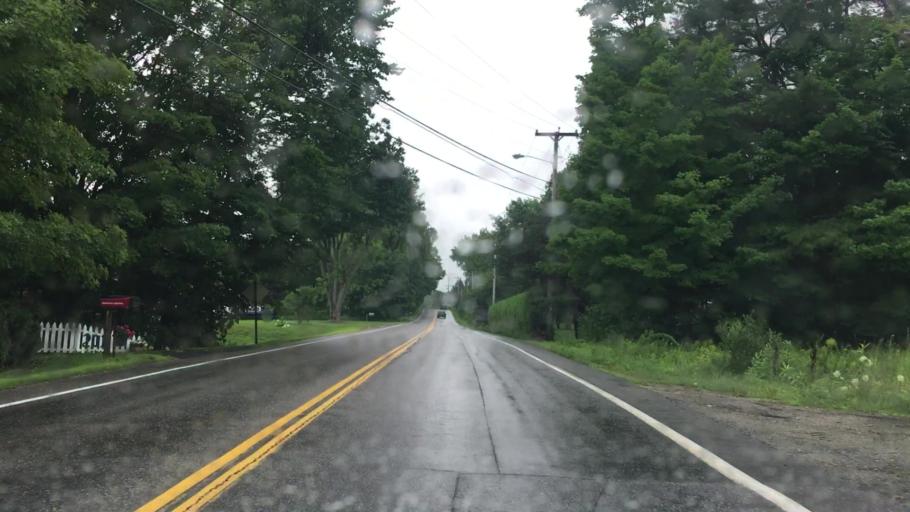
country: US
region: Maine
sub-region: Kennebec County
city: Augusta
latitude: 44.3340
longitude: -69.8158
